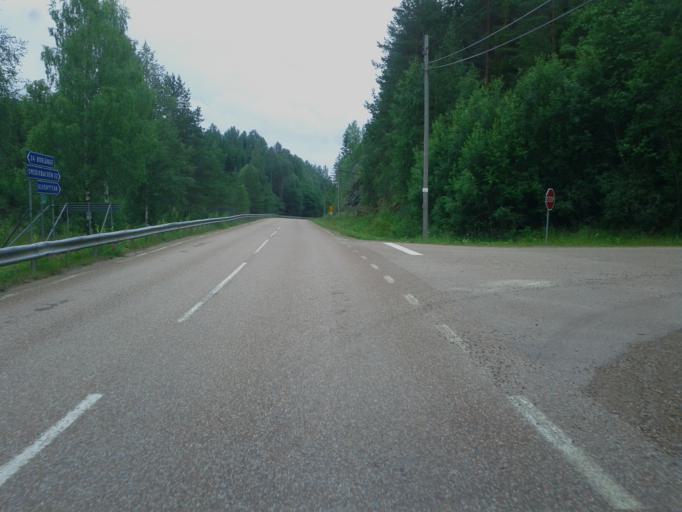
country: SE
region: Dalarna
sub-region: Borlange Kommun
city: Borlaenge
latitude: 60.3184
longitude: 15.3760
